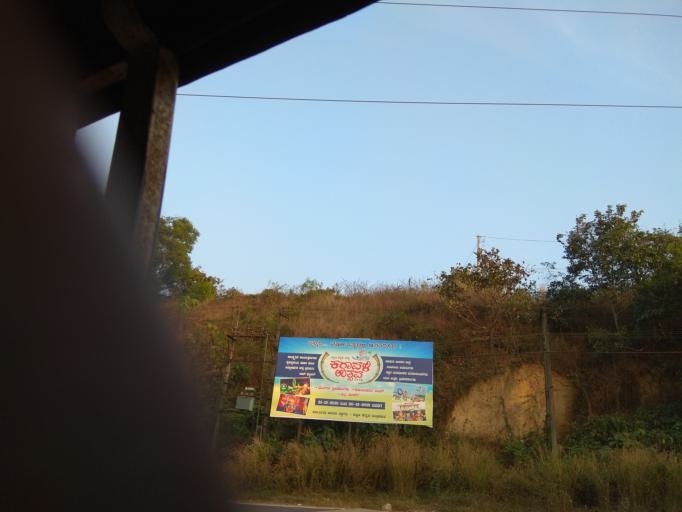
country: IN
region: Karnataka
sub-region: Dakshina Kannada
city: Mangalore
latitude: 12.9358
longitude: 74.8602
